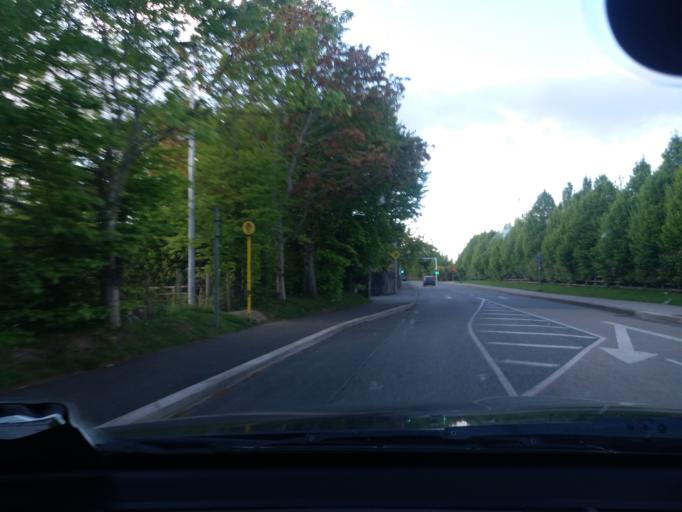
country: IE
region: Leinster
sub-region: South Dublin
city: Saggart
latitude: 53.2837
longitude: -6.4409
